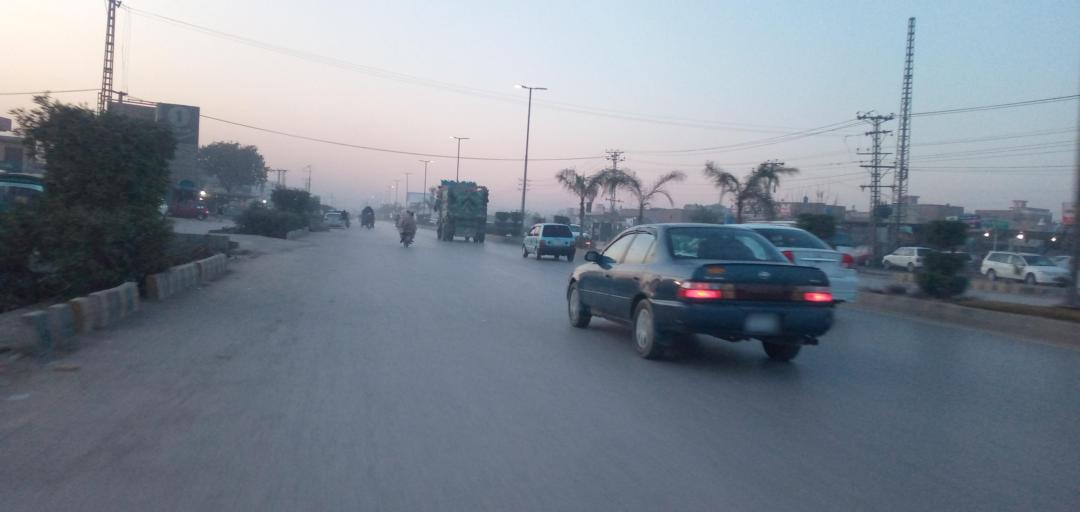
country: PK
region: Khyber Pakhtunkhwa
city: Peshawar
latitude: 34.0299
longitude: 71.6117
